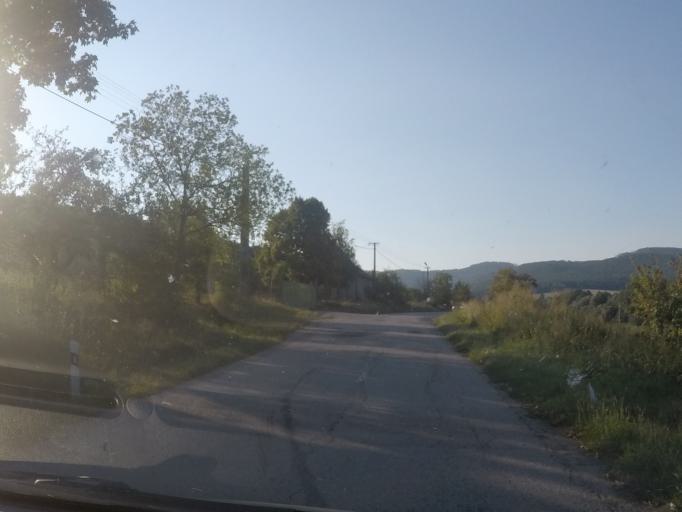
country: SK
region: Nitriansky
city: Zlate Moravce
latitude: 48.4565
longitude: 18.3196
